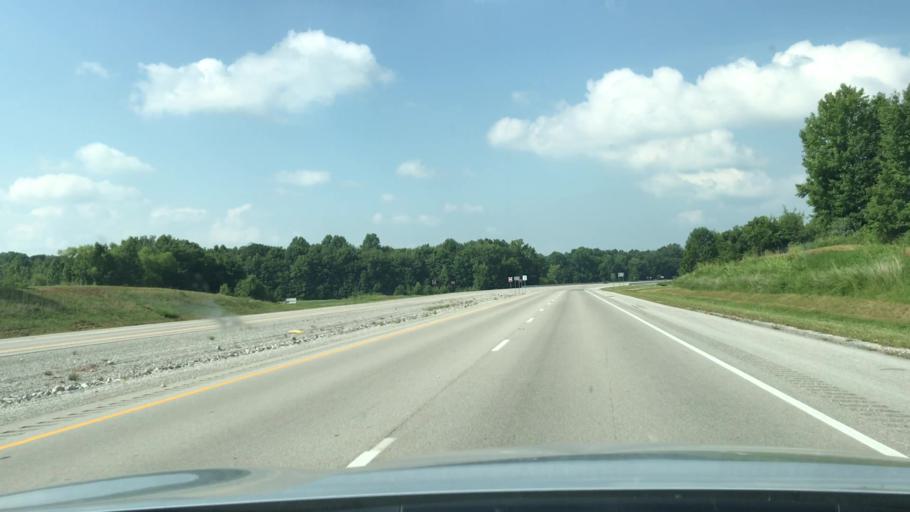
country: US
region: Kentucky
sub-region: Barren County
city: Glasgow
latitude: 37.0043
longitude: -85.9599
